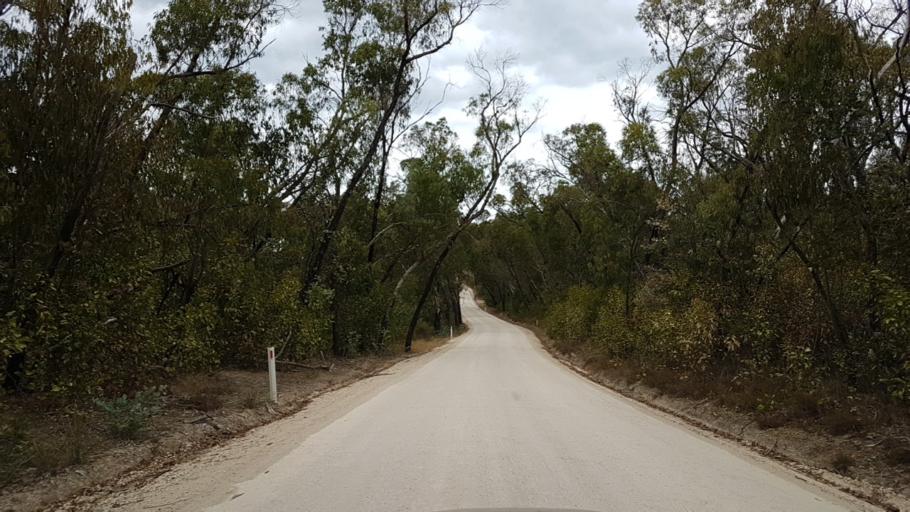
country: AU
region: South Australia
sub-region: Adelaide Hills
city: Gumeracha
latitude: -34.7917
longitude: 138.8354
